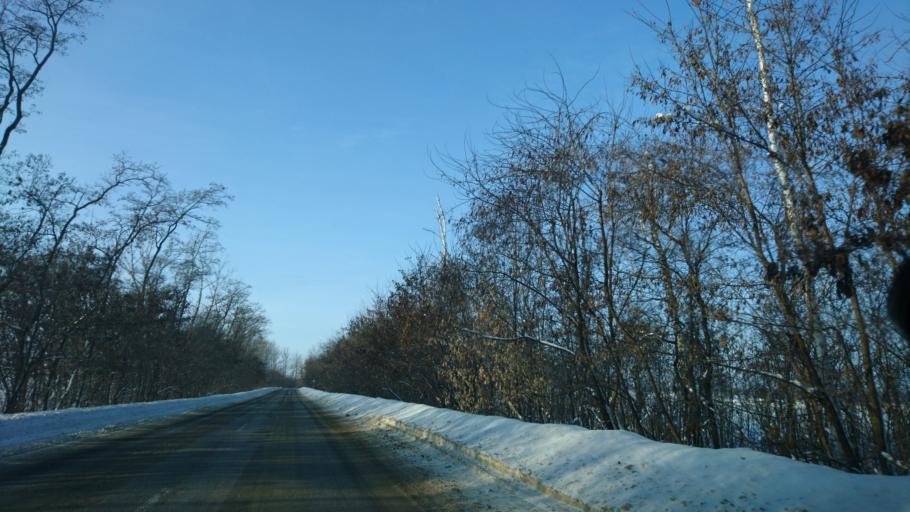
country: RU
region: Belgorod
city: Severnyy
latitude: 50.7265
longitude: 36.5627
